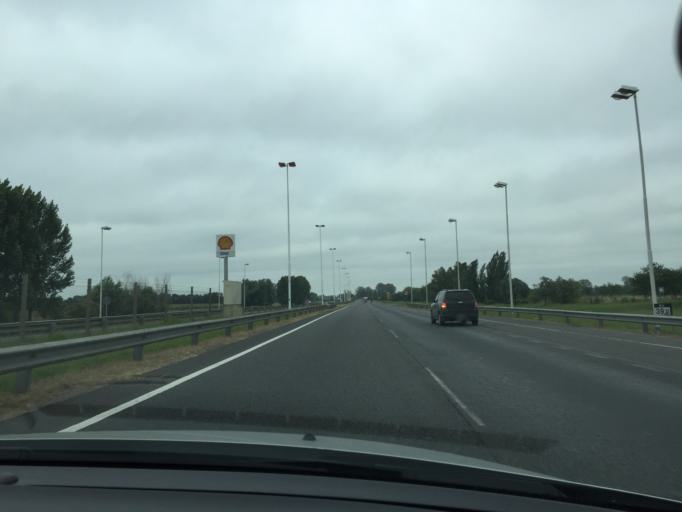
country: AR
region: Buenos Aires
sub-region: Partido de Ezeiza
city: Ezeiza
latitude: -34.8620
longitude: -58.5674
